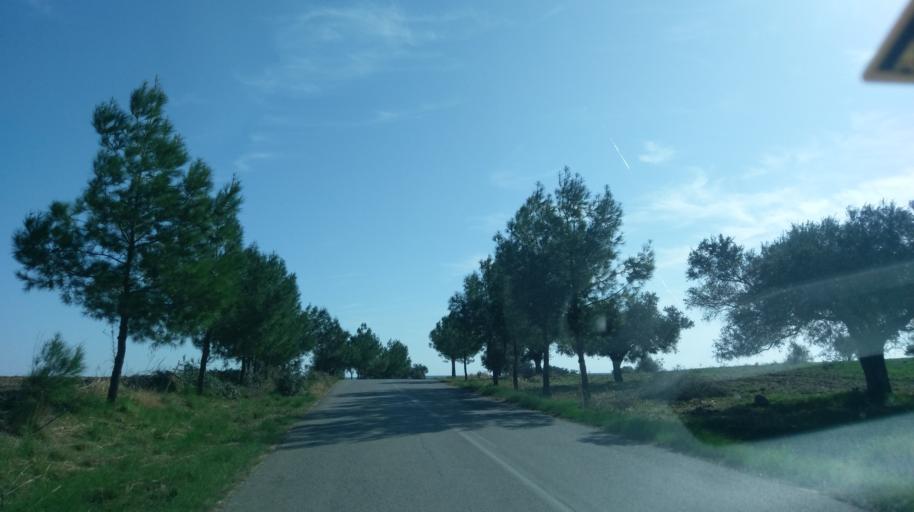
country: CY
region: Ammochostos
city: Trikomo
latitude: 35.3864
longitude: 33.9999
